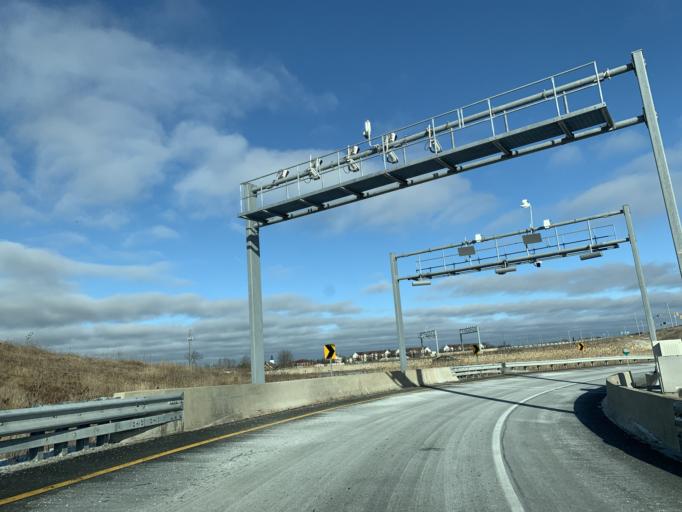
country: CA
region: Ontario
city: Mississauga
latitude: 43.5523
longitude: -79.7646
